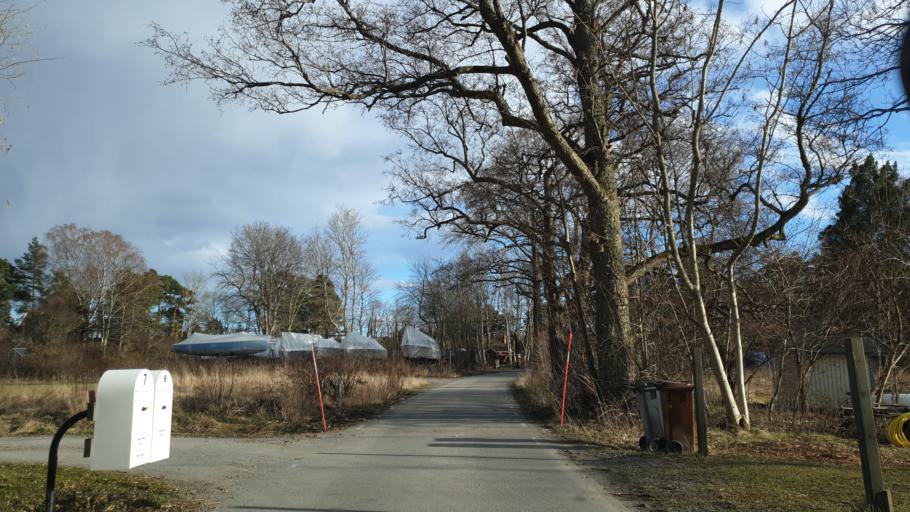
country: SE
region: Stockholm
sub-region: Varmdo Kommun
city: Holo
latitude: 59.3081
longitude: 18.6914
